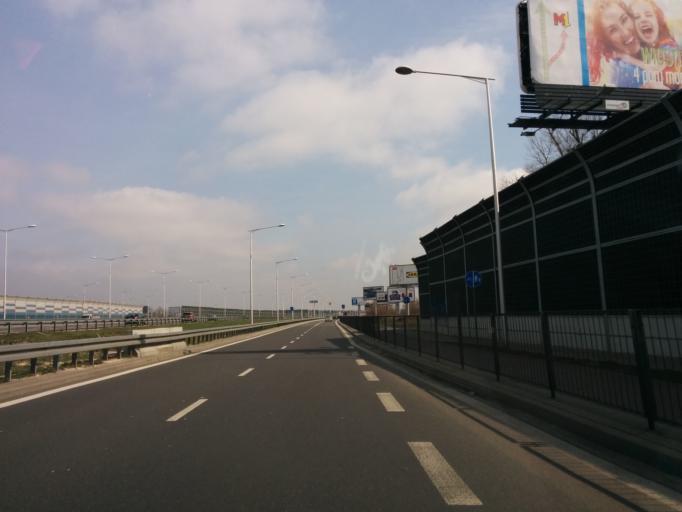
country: PL
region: Masovian Voivodeship
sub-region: Warszawa
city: Targowek
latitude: 52.3068
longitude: 21.0633
